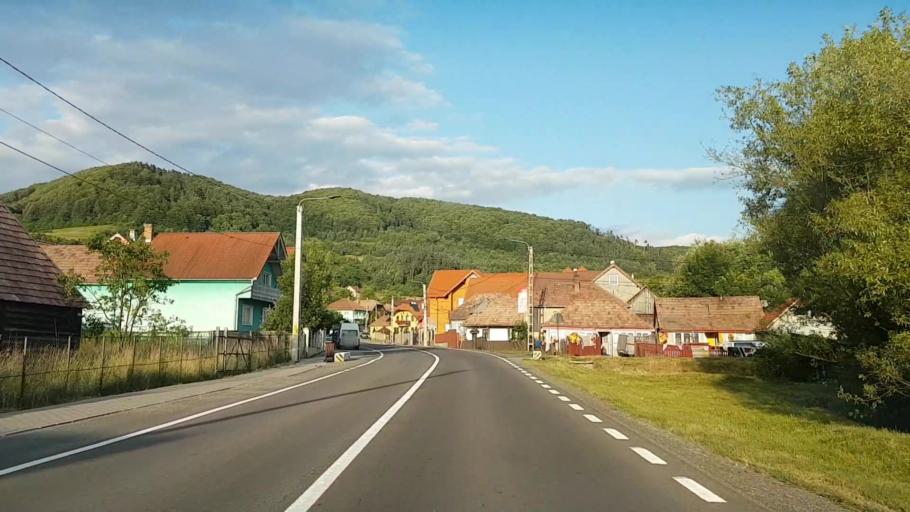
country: RO
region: Harghita
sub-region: Comuna Corund
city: Corund
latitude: 46.4697
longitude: 25.1946
